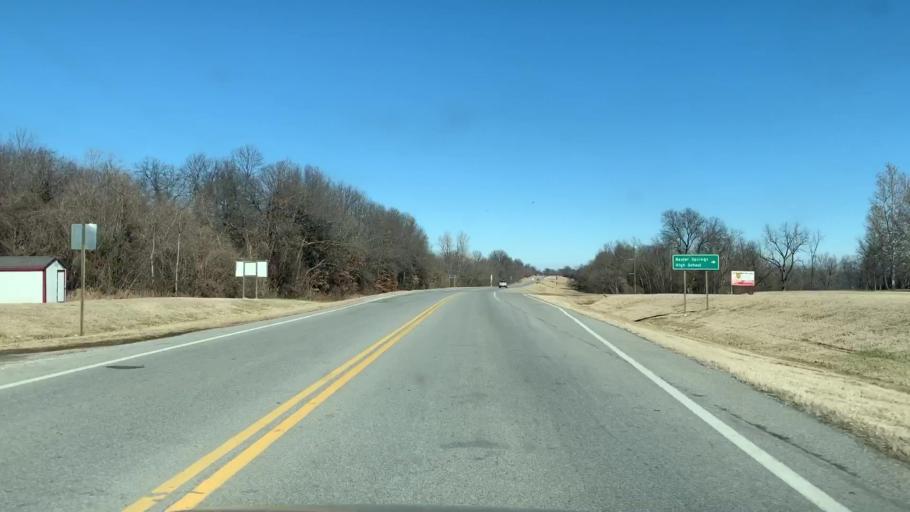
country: US
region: Kansas
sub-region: Cherokee County
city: Baxter Springs
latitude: 37.0369
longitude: -94.7350
